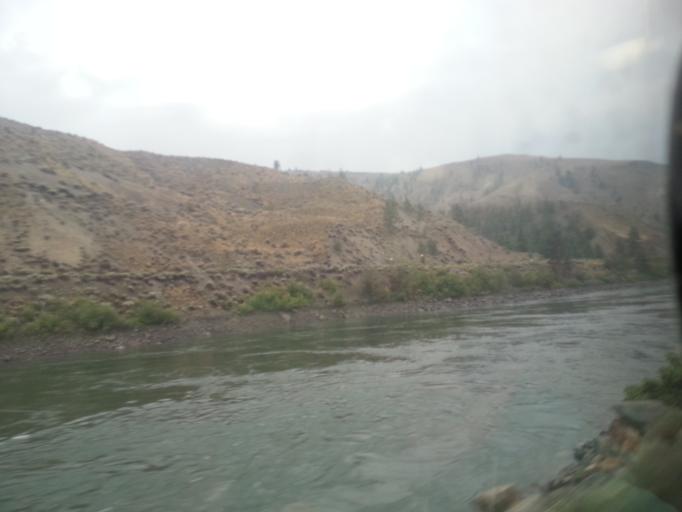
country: CA
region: British Columbia
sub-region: Thompson-Nicola Regional District
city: Ashcroft
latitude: 50.5042
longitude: -121.2846
